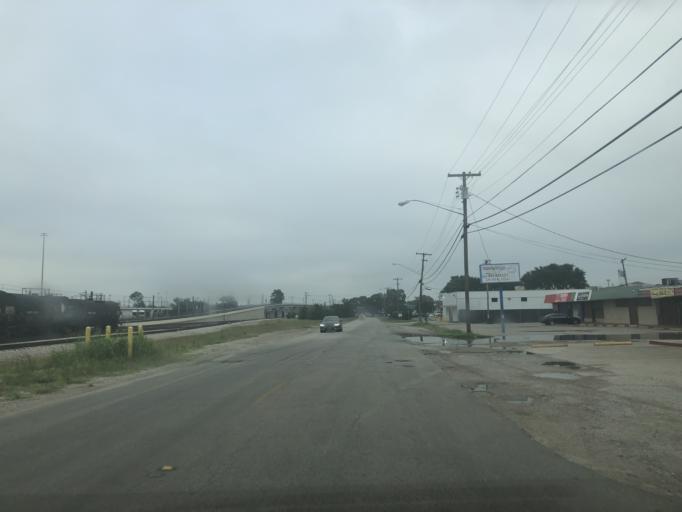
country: US
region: Texas
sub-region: Dallas County
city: Farmers Branch
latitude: 32.8693
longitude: -96.8805
